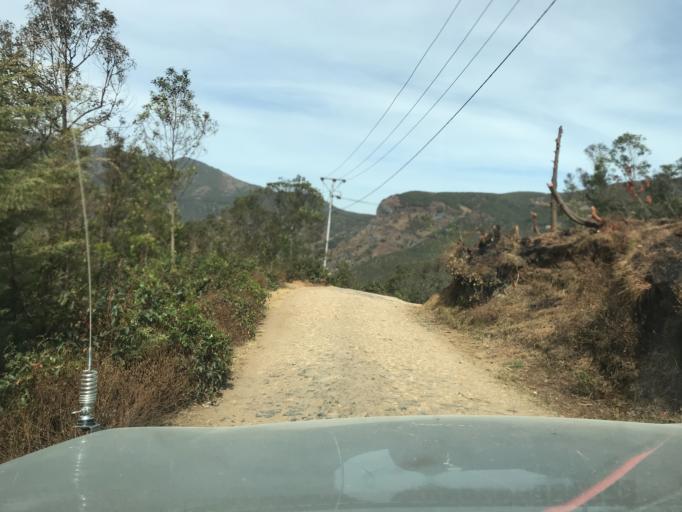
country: TL
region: Ainaro
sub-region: Ainaro
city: Ainaro
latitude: -8.8854
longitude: 125.5344
